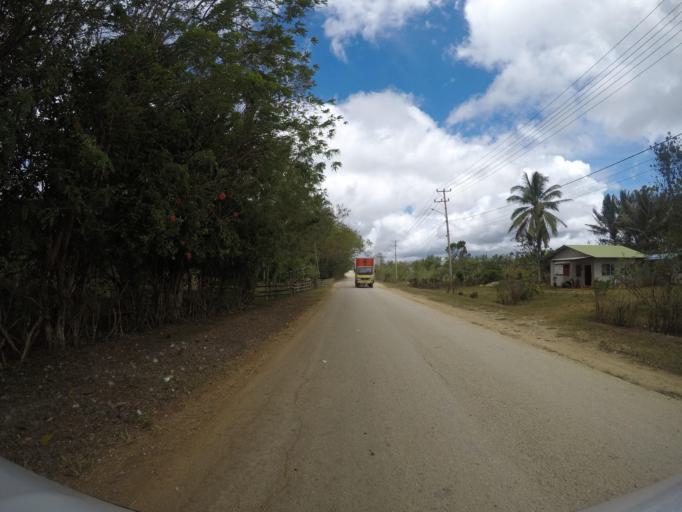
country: TL
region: Lautem
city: Lospalos
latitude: -8.4745
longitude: 126.9929
